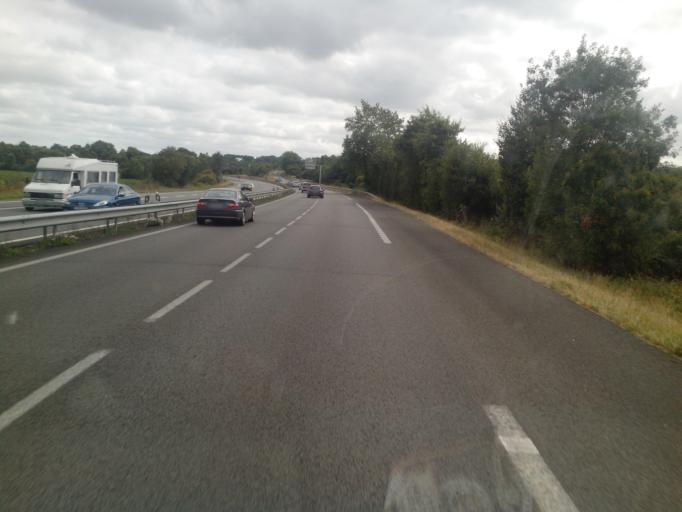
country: FR
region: Pays de la Loire
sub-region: Departement de la Loire-Atlantique
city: Heric
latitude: 47.4205
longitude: -1.6403
